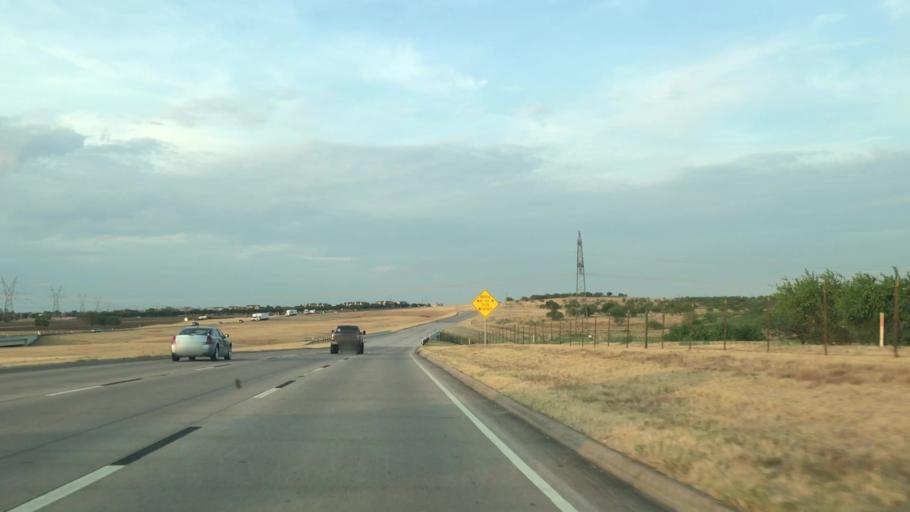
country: US
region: Texas
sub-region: Tarrant County
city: Keller
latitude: 32.9654
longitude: -97.2948
